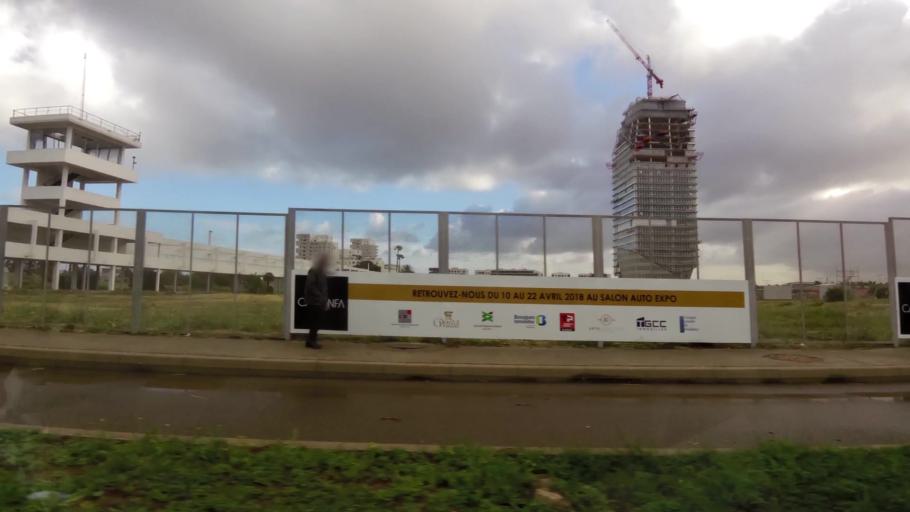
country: MA
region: Grand Casablanca
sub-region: Casablanca
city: Casablanca
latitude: 33.5619
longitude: -7.6625
